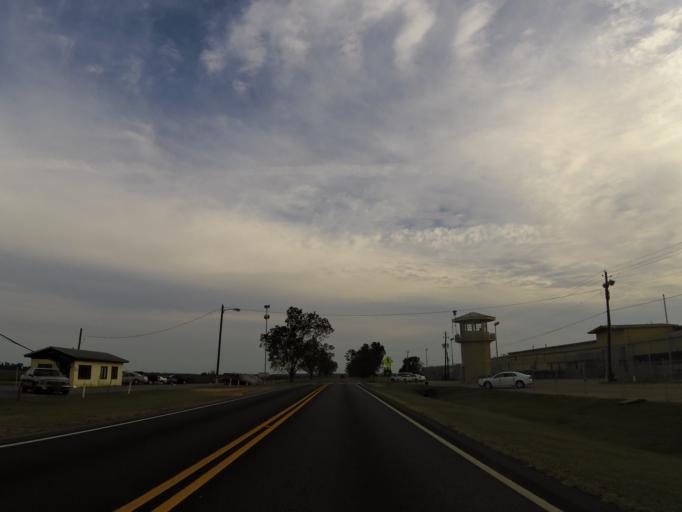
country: US
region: Alabama
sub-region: Escambia County
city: Atmore
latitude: 31.1576
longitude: -87.4636
